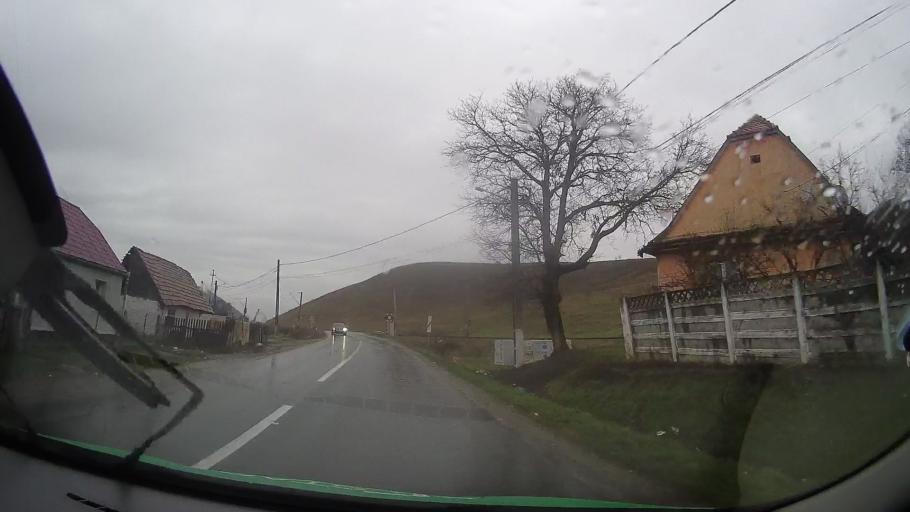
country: RO
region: Bistrita-Nasaud
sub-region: Comuna Mariselu
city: Mariselu
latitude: 47.0424
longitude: 24.4712
